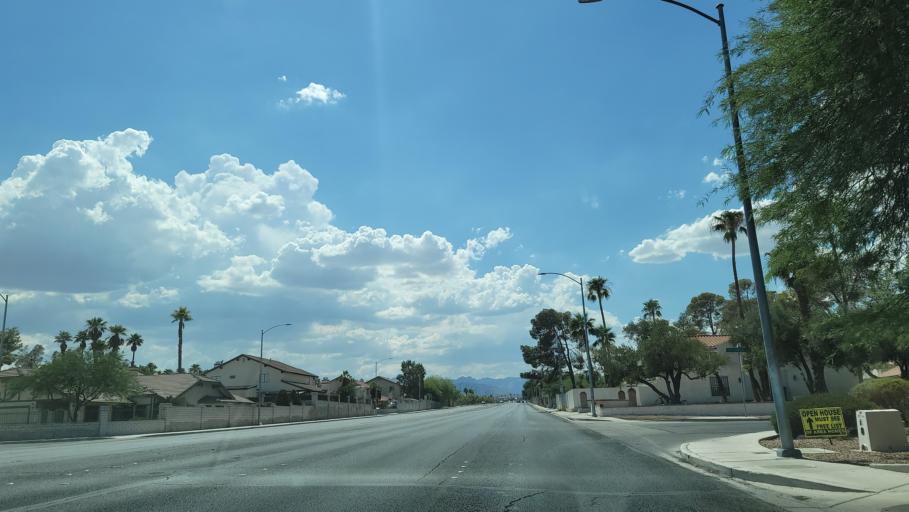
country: US
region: Nevada
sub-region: Clark County
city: Spring Valley
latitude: 36.1296
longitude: -115.2453
